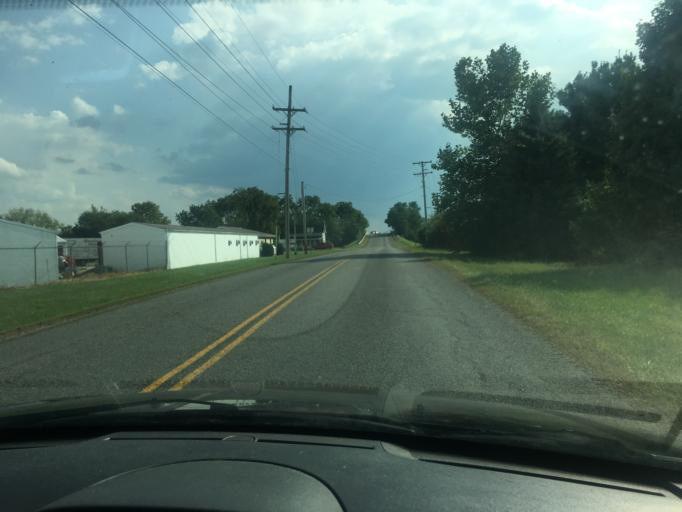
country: US
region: Ohio
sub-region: Champaign County
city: Urbana
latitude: 40.0994
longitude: -83.7711
